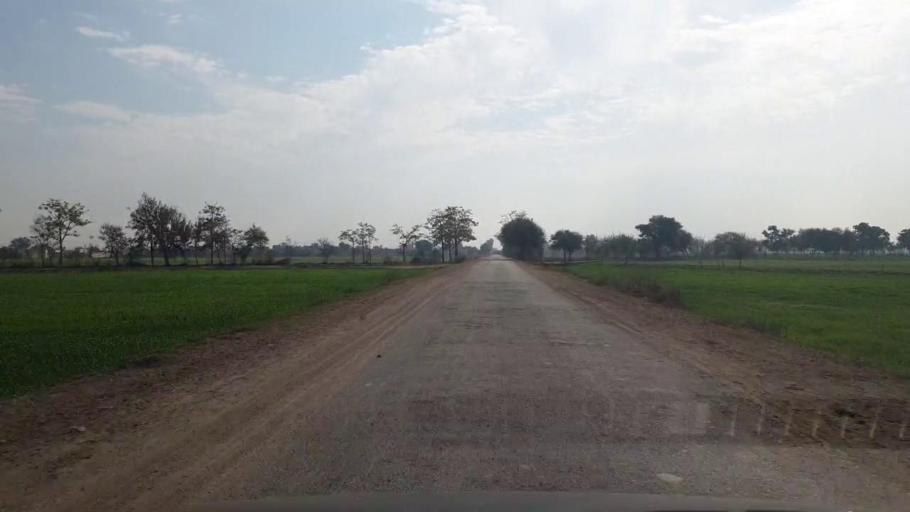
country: PK
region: Sindh
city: Hala
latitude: 25.9958
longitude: 68.4163
